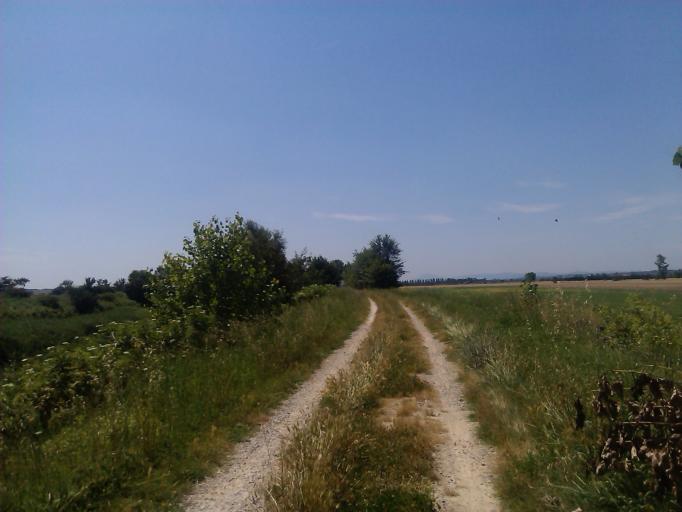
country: IT
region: Tuscany
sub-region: Province of Arezzo
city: Cesa
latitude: 43.3442
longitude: 11.8265
